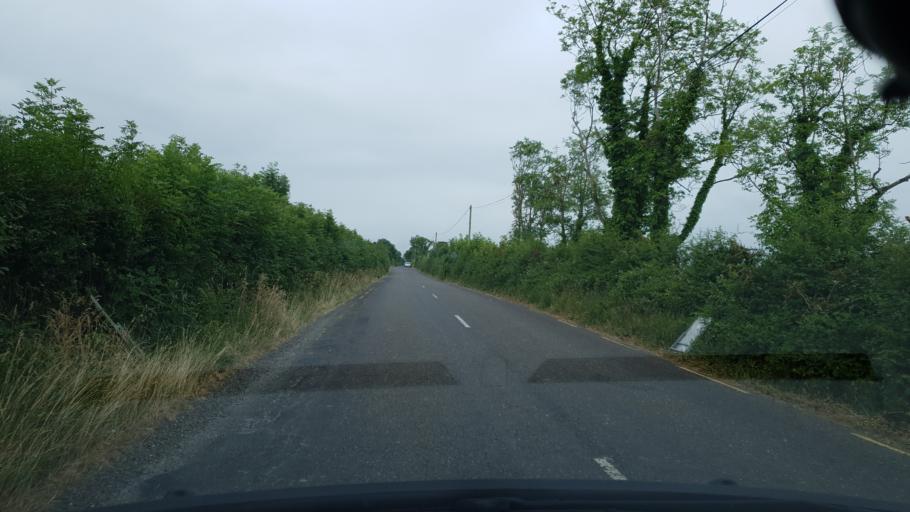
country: IE
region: Munster
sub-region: Ciarrai
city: Tralee
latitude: 52.1627
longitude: -9.6434
